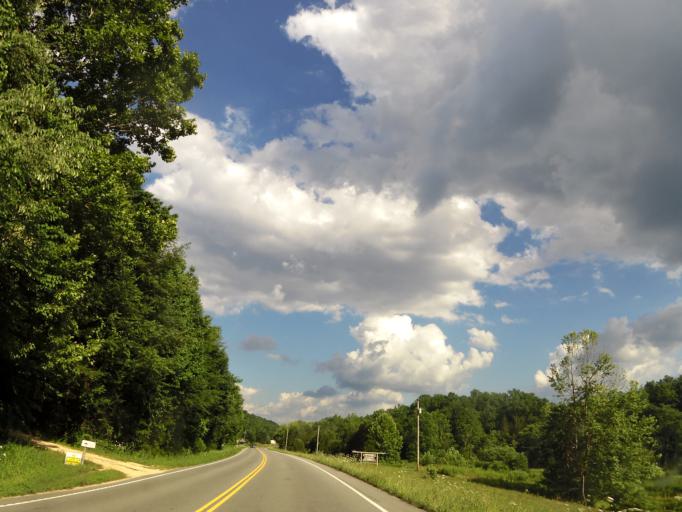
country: US
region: Tennessee
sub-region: Perry County
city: Linden
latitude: 35.5988
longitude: -87.7004
